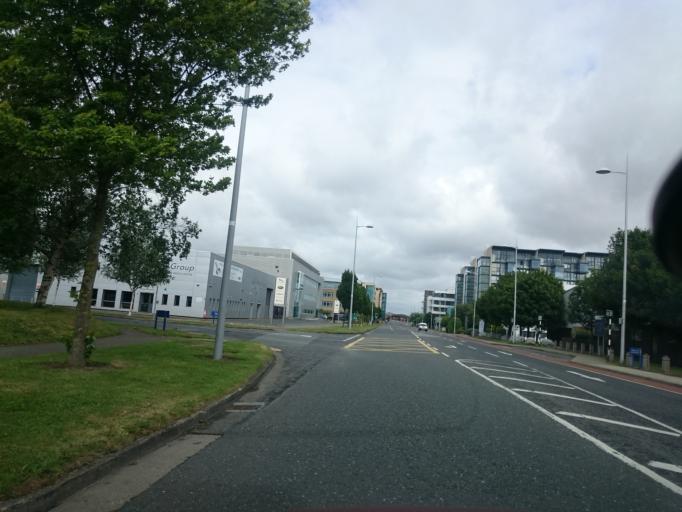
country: IE
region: Leinster
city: Sandyford
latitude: 53.2752
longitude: -6.2142
